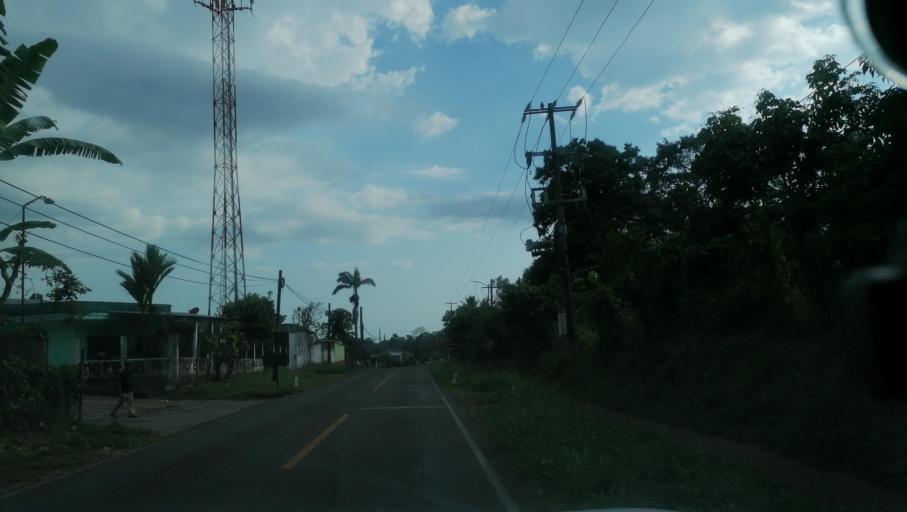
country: MX
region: Chiapas
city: Cacahoatan
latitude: 15.0094
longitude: -92.1557
